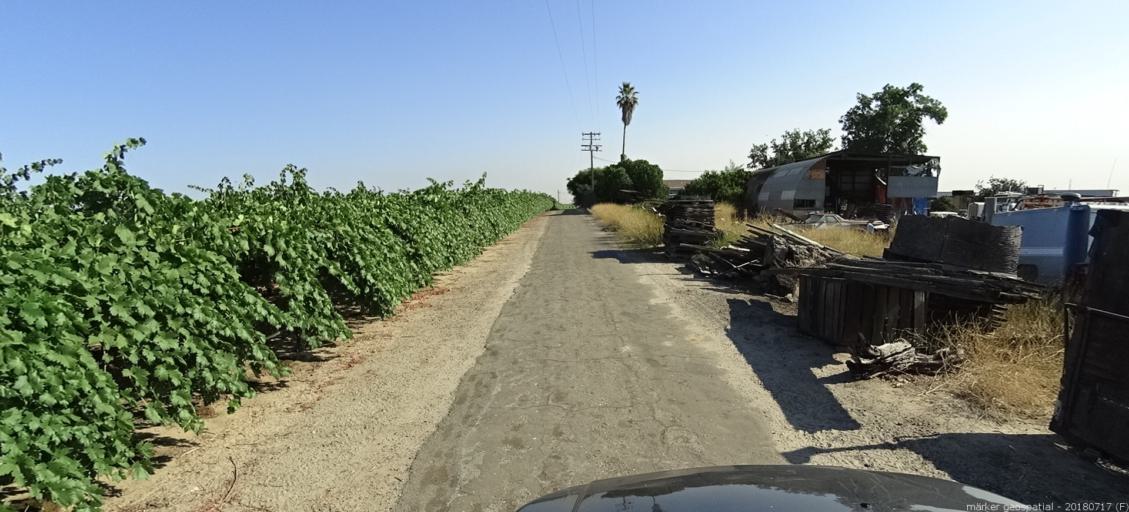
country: US
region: California
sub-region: Madera County
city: Madera Acres
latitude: 37.0451
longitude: -120.1266
